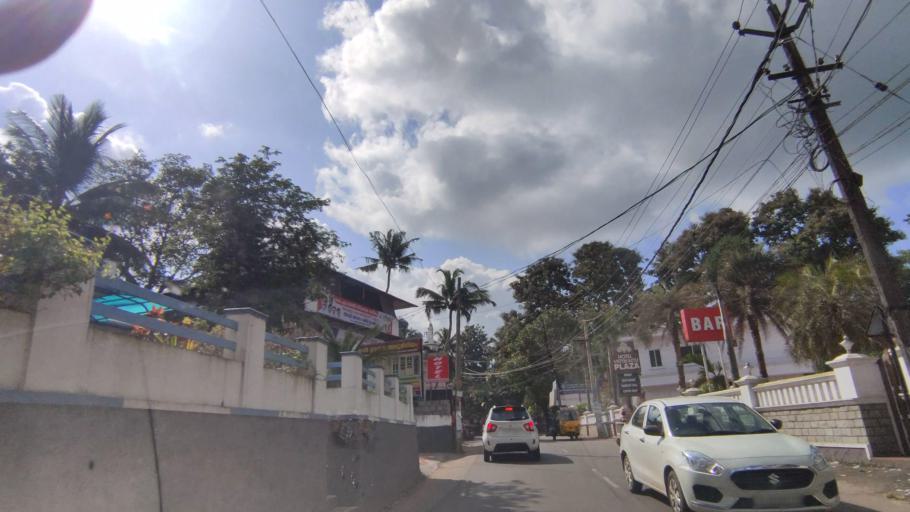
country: IN
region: Kerala
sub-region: Kottayam
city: Kottayam
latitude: 9.6859
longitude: 76.5053
